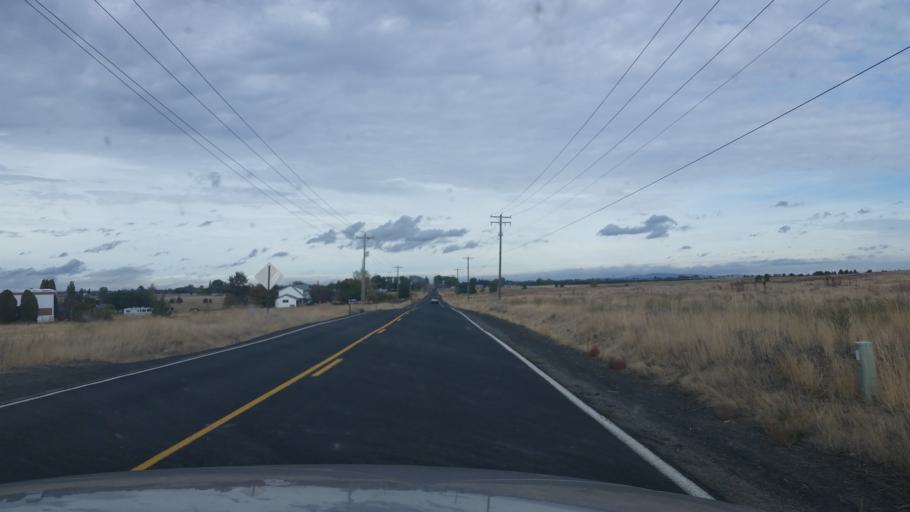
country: US
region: Washington
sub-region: Spokane County
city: Fairchild Air Force Base
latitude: 47.5955
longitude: -117.6075
